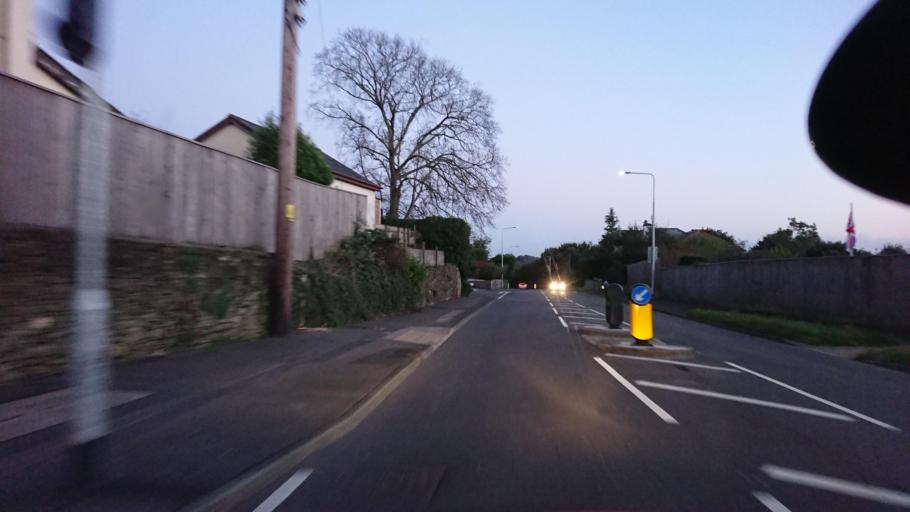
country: GB
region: England
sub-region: Plymouth
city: Plymouth
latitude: 50.4036
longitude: -4.1187
